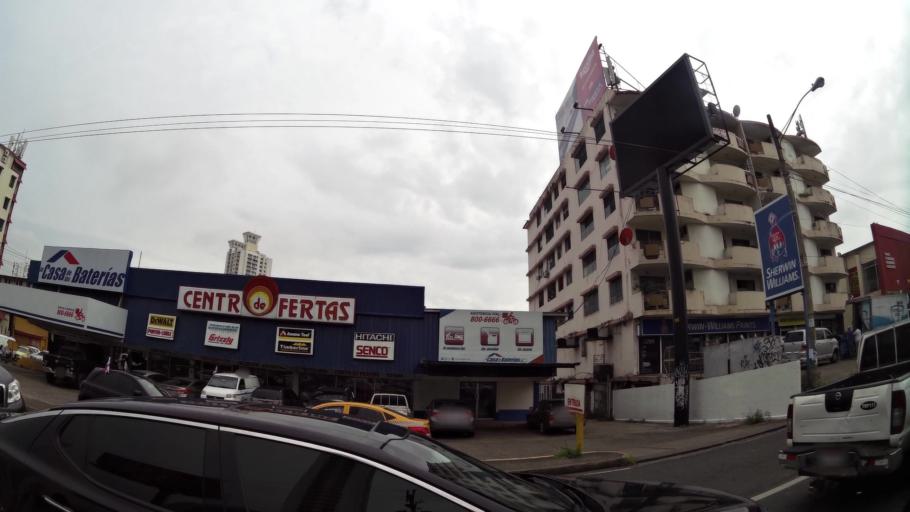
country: PA
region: Panama
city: Panama
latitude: 8.9932
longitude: -79.5200
